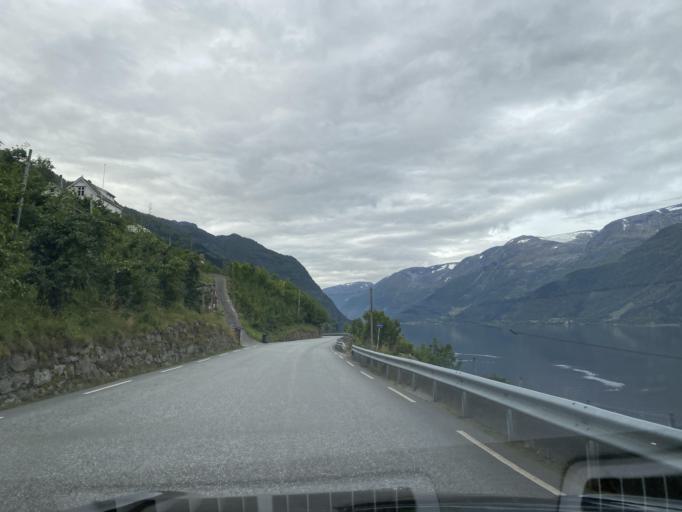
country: NO
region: Hordaland
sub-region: Odda
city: Odda
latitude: 60.2128
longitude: 6.6030
